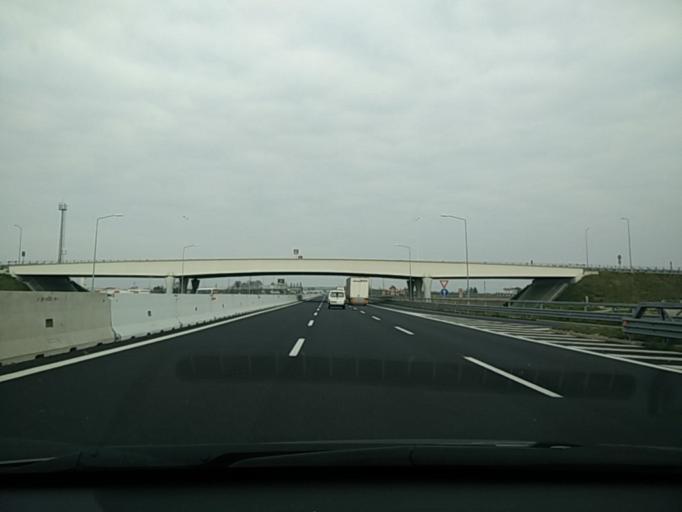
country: IT
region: Veneto
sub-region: Provincia di Venezia
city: Meolo
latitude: 45.6270
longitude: 12.4379
